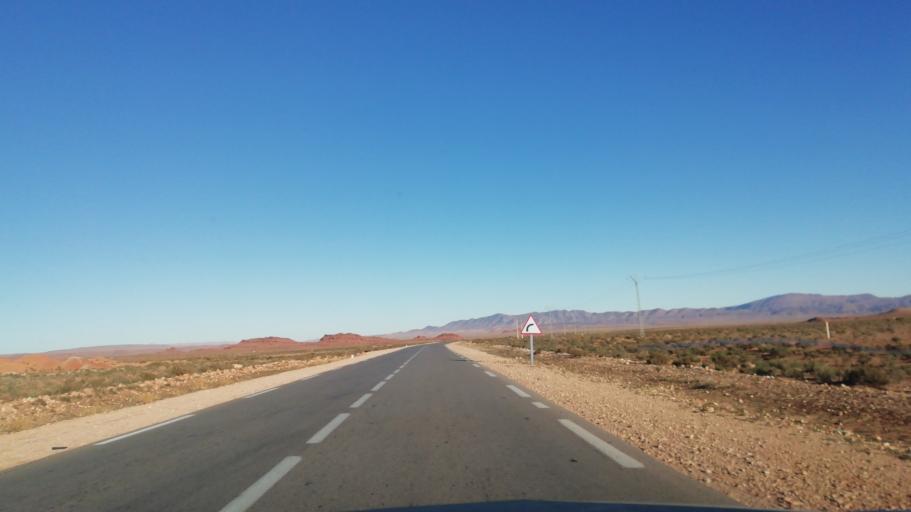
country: DZ
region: El Bayadh
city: El Abiodh Sidi Cheikh
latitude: 33.1702
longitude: 0.4883
